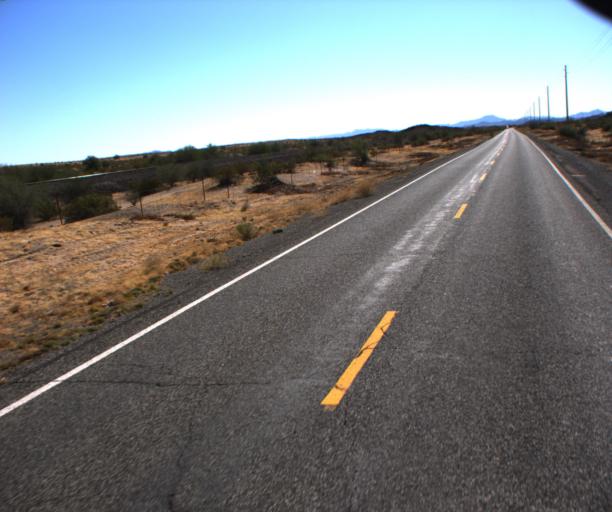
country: US
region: Arizona
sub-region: La Paz County
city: Cienega Springs
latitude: 33.9931
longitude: -114.0903
